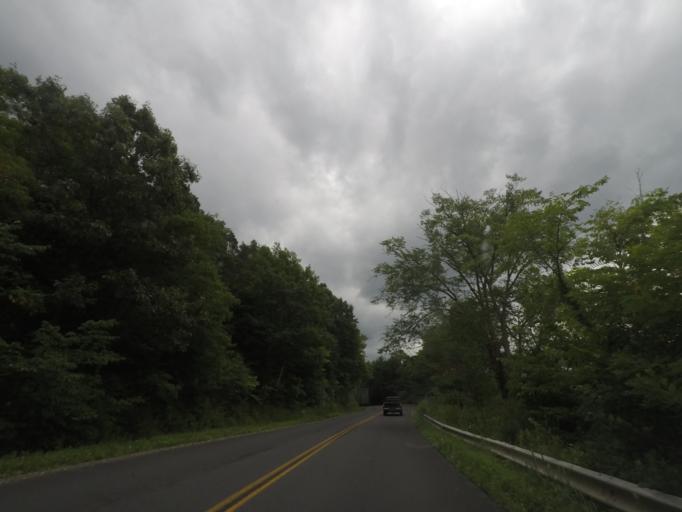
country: US
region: New York
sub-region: Rensselaer County
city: Poestenkill
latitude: 42.8272
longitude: -73.5191
